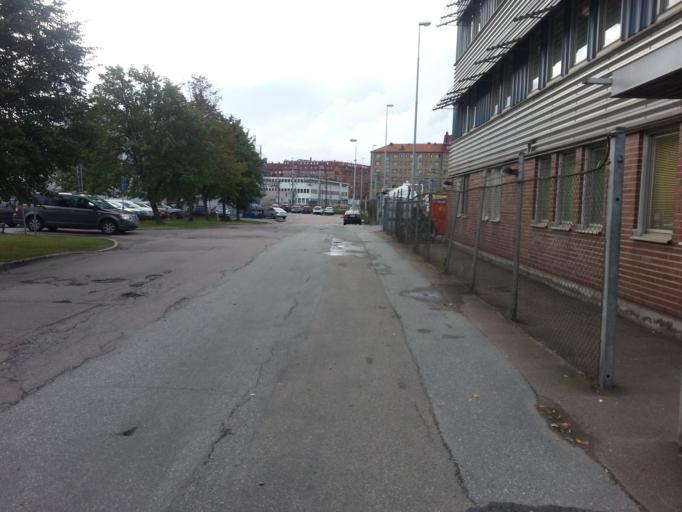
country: SE
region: Vaestra Goetaland
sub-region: Goteborg
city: Goeteborg
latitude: 57.7116
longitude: 11.9799
